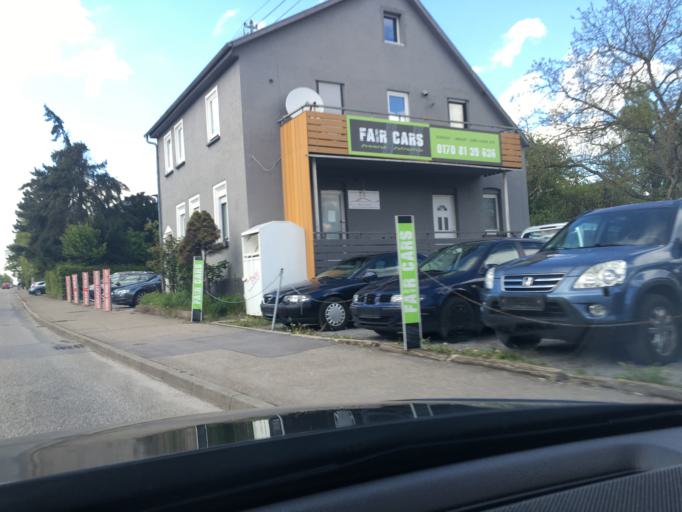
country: DE
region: Baden-Wuerttemberg
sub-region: Regierungsbezirk Stuttgart
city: Waiblingen
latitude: 48.8538
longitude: 9.2959
